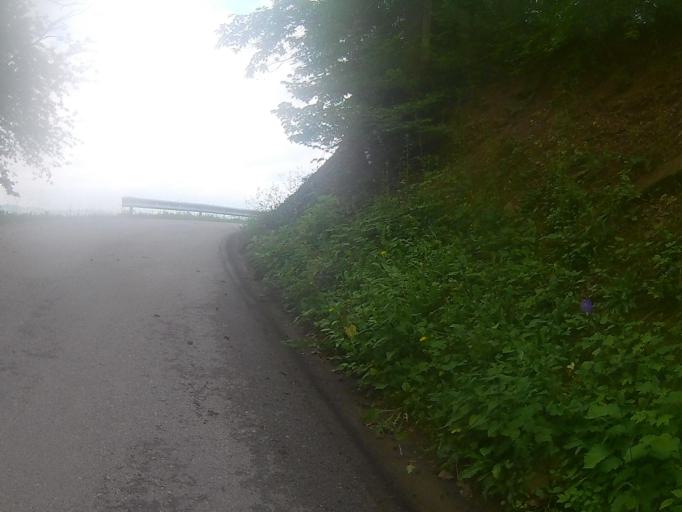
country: SI
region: Kungota
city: Zgornja Kungota
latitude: 46.6261
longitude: 15.5929
